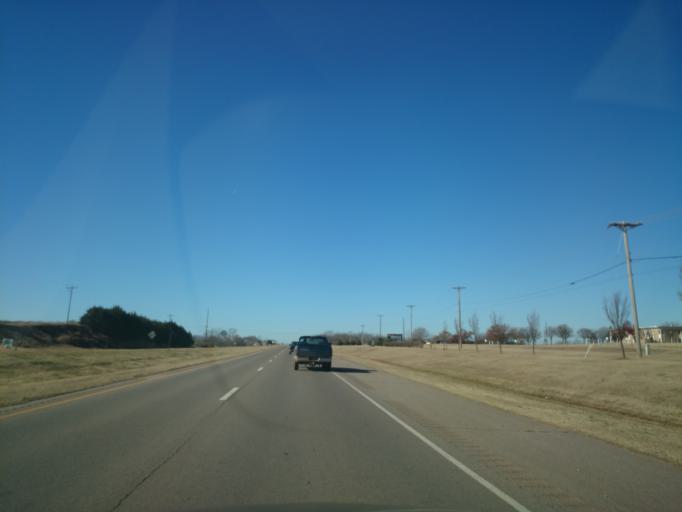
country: US
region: Oklahoma
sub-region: Payne County
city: Stillwater
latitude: 36.1161
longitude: -97.1366
